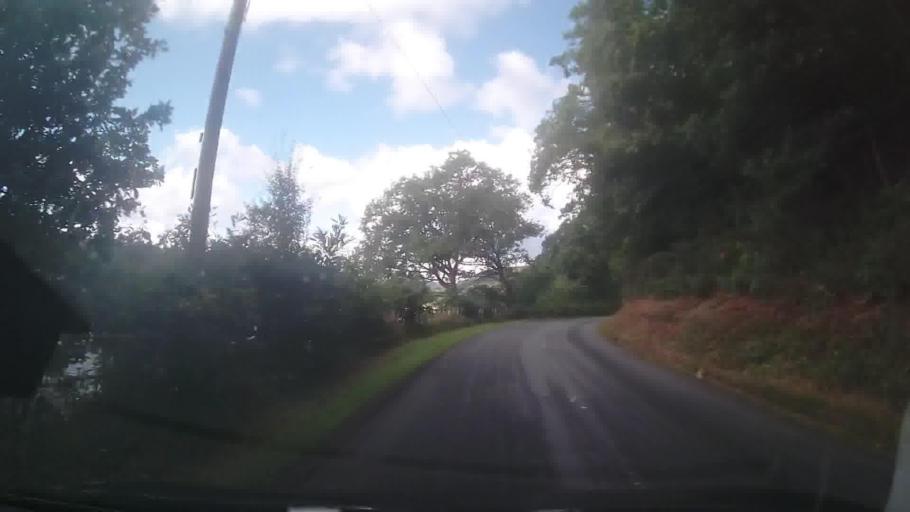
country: GB
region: Wales
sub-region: Sir Powys
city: Llangynog
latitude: 52.7742
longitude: -3.4718
